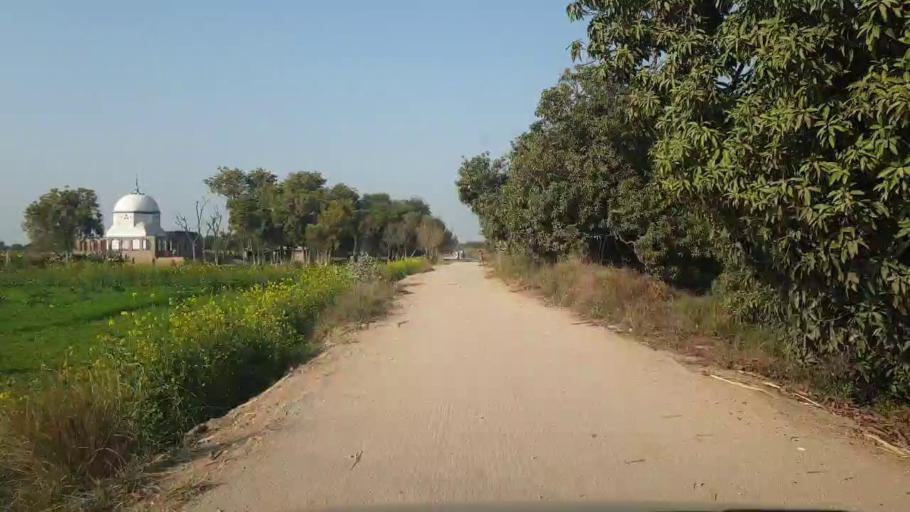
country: PK
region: Sindh
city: Bhit Shah
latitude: 25.8267
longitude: 68.5200
